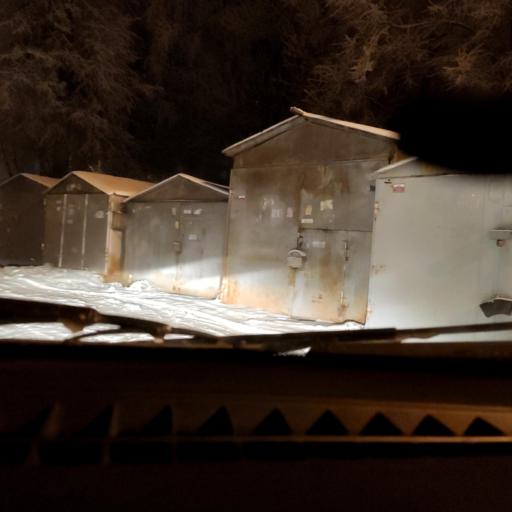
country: RU
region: Bashkortostan
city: Ufa
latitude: 54.7662
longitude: 55.9997
